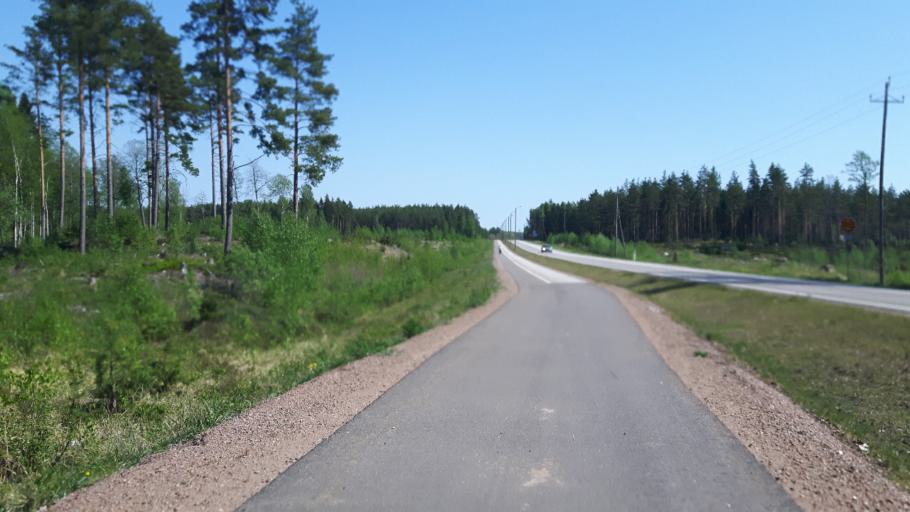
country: FI
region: Kymenlaakso
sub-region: Kotka-Hamina
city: Pyhtaeae
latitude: 60.4886
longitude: 26.5112
